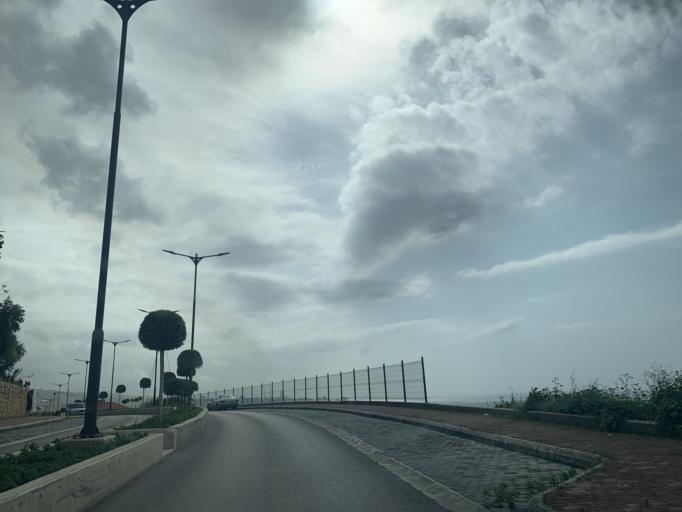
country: LB
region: Mont-Liban
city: Djounie
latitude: 33.9993
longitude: 35.6478
